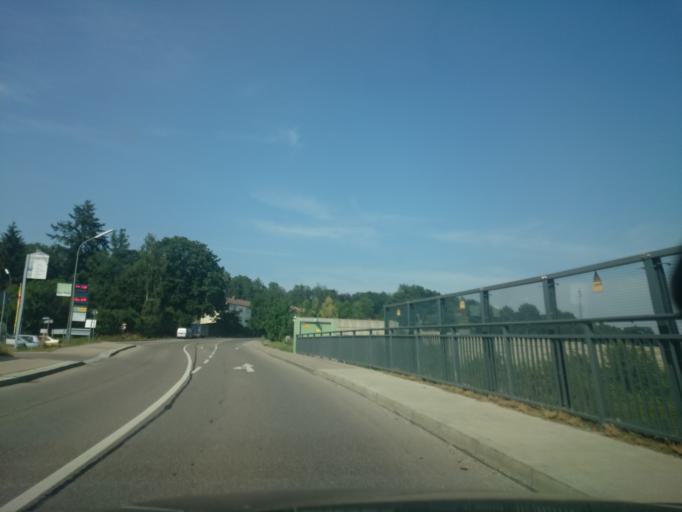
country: DE
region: Bavaria
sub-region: Upper Bavaria
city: Althegnenberg
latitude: 48.2337
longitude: 11.0703
